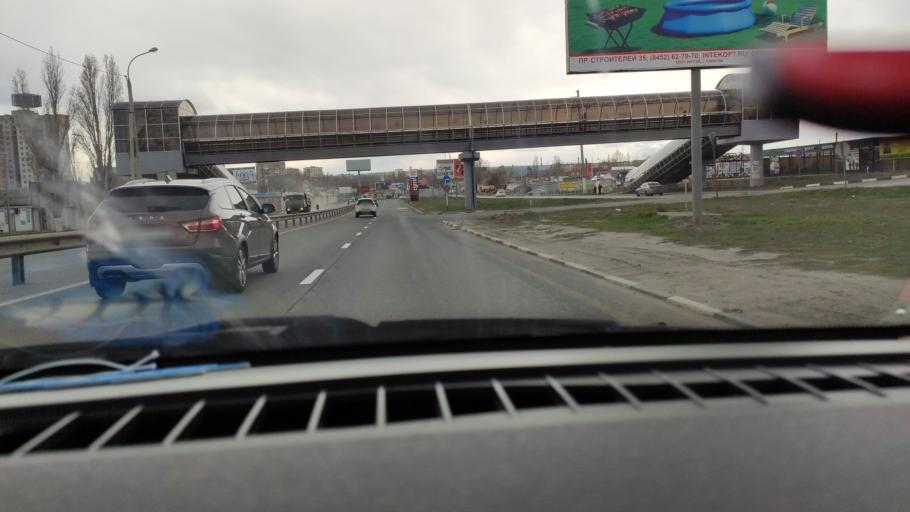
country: RU
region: Saratov
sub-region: Saratovskiy Rayon
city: Saratov
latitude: 51.6164
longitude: 45.9723
